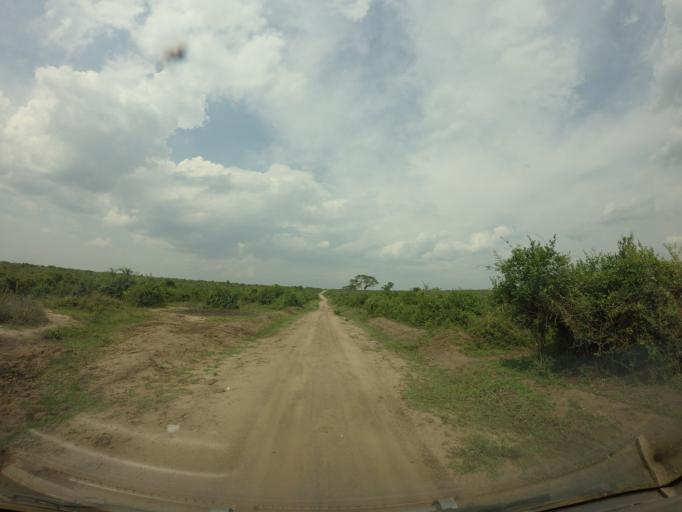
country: UG
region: Western Region
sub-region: Rubirizi District
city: Rubirizi
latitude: -0.2099
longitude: 29.9121
